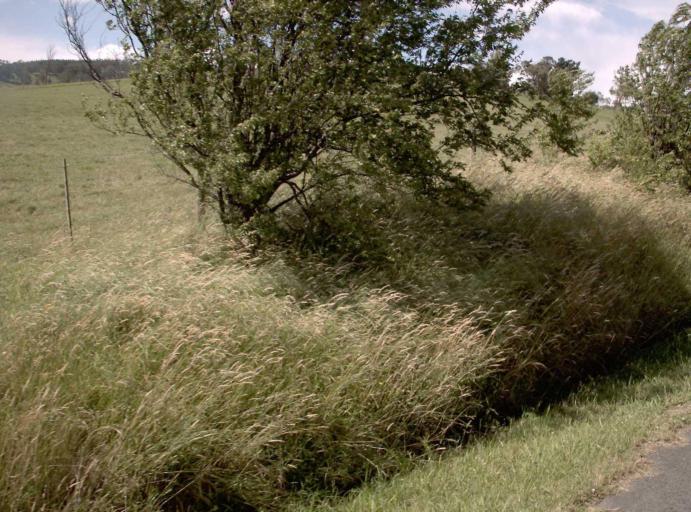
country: AU
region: Victoria
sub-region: Latrobe
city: Traralgon
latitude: -38.1502
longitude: 146.4701
